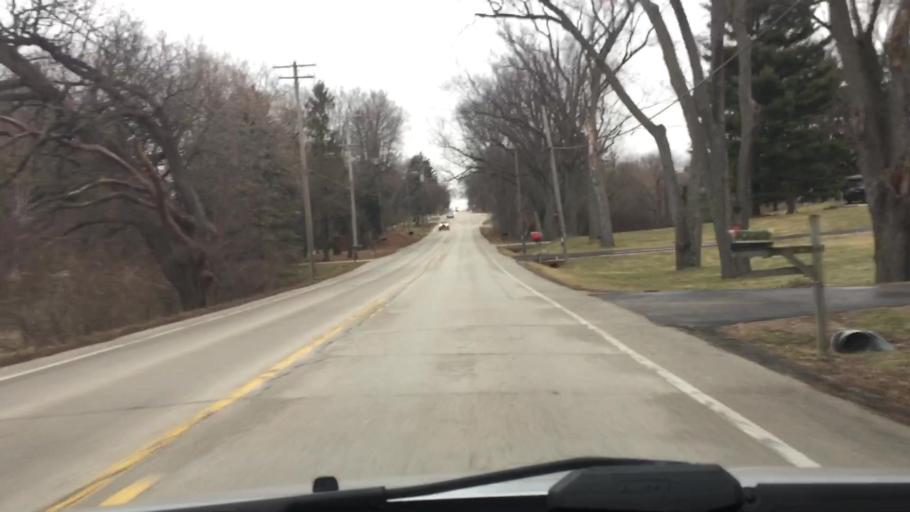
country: US
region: Wisconsin
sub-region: Waukesha County
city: Nashotah
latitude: 43.0924
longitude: -88.4031
